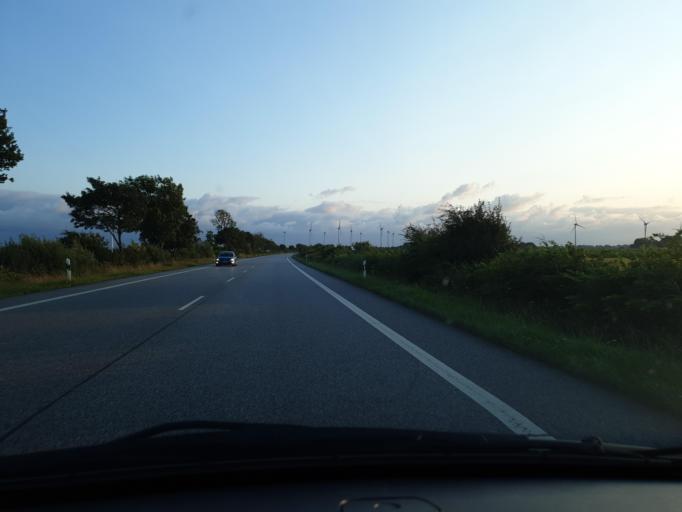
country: DE
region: Schleswig-Holstein
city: Brunsbuttel
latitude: 53.9124
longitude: 9.1145
